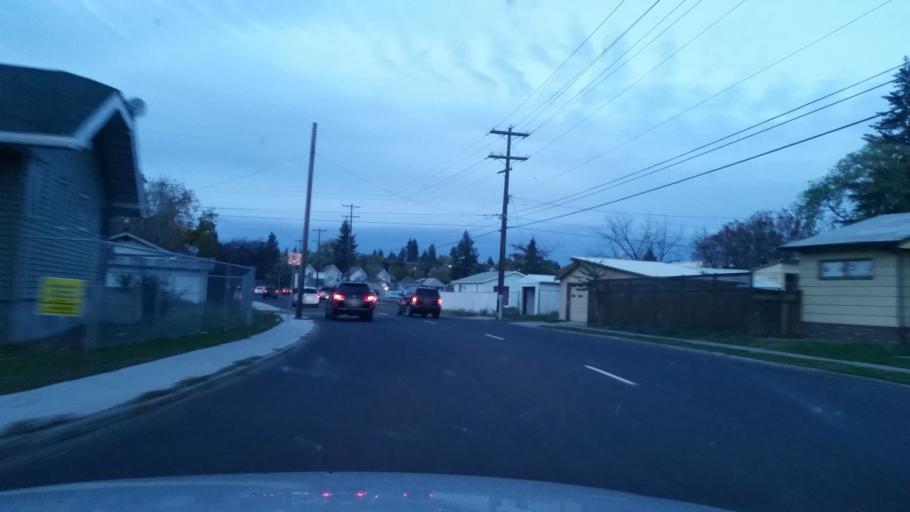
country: US
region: Washington
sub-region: Spokane County
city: Spokane
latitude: 47.6826
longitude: -117.4355
